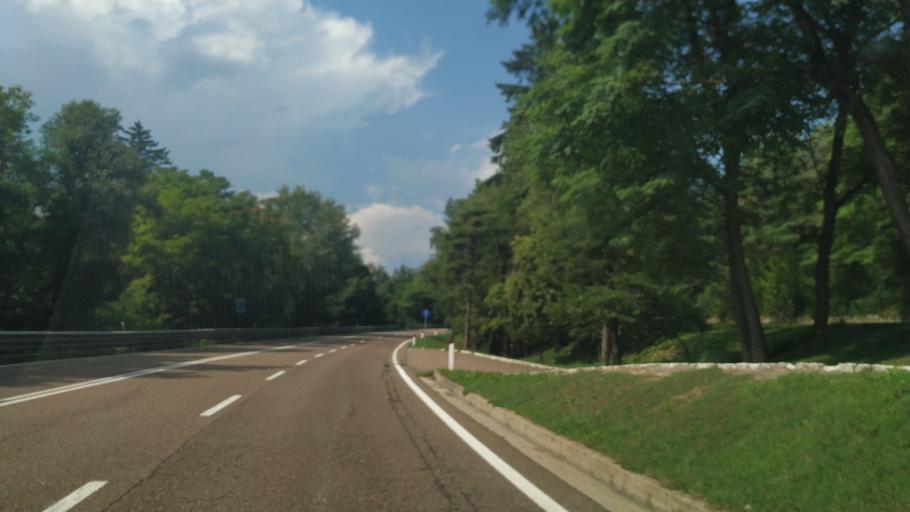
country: IT
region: Trentino-Alto Adige
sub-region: Provincia di Trento
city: Denno
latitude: 46.2815
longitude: 11.0621
